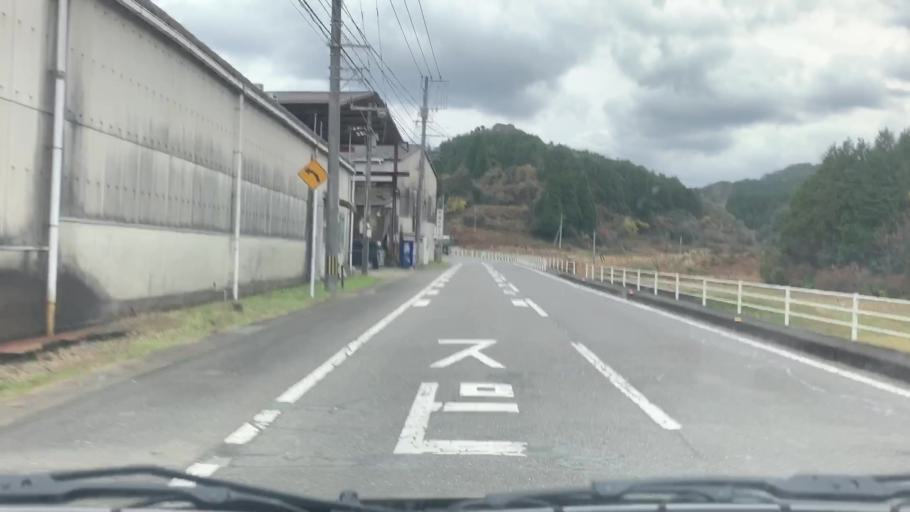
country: JP
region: Saga Prefecture
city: Ureshinomachi-shimojuku
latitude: 33.1332
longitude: 129.9737
